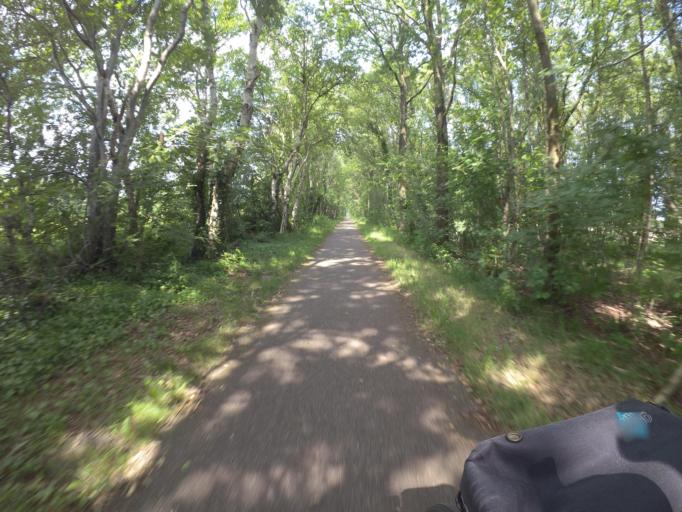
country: NL
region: Drenthe
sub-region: Gemeente Assen
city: Assen
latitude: 52.9268
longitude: 6.5030
